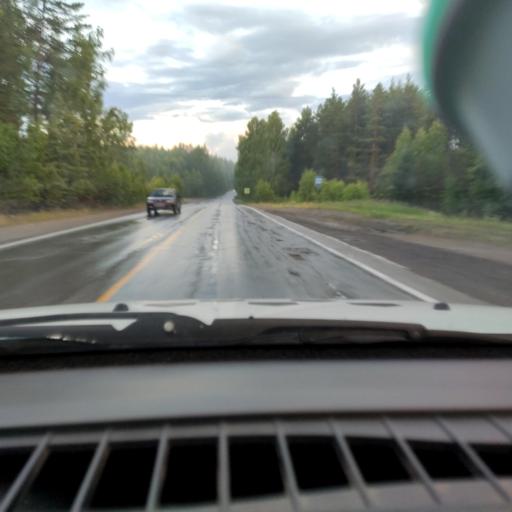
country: RU
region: Chelyabinsk
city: Kyshtym
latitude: 55.7546
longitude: 60.5535
